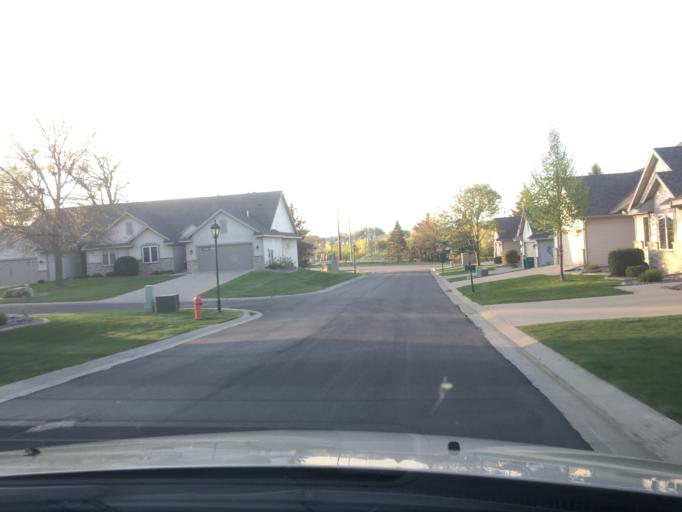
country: US
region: Minnesota
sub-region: Olmsted County
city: Oronoco
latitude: 44.0785
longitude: -92.5376
